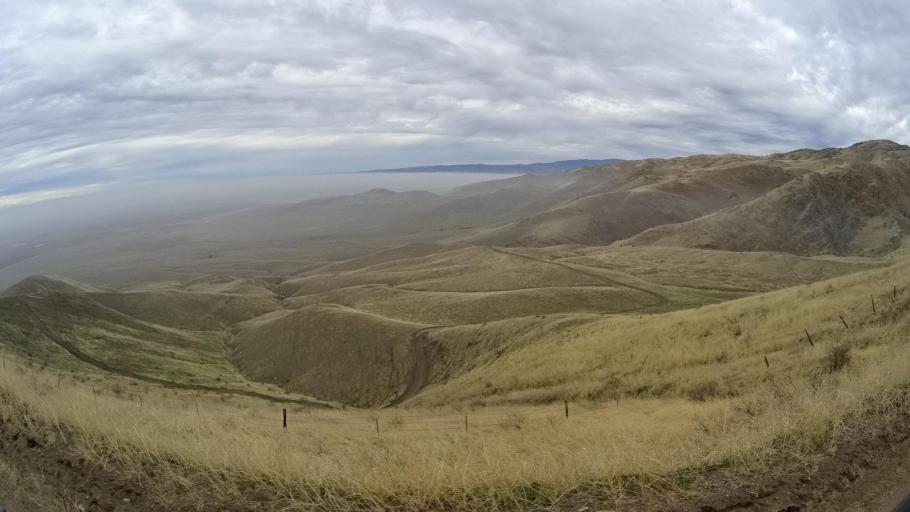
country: US
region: California
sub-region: Kern County
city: Arvin
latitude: 35.1397
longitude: -118.7843
